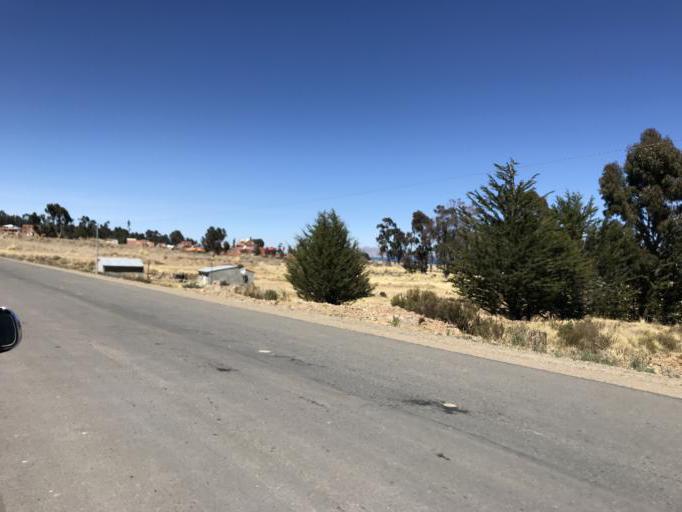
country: BO
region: La Paz
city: Huatajata
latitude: -16.1945
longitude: -68.7252
